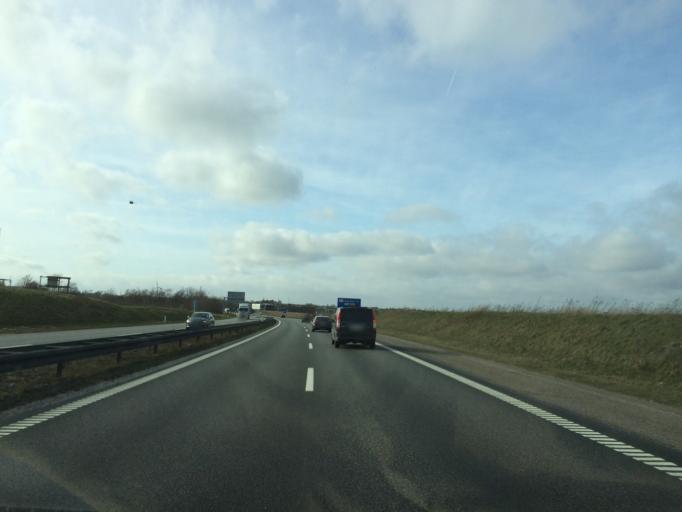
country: DK
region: Central Jutland
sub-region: Randers Kommune
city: Randers
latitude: 56.4183
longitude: 10.0711
